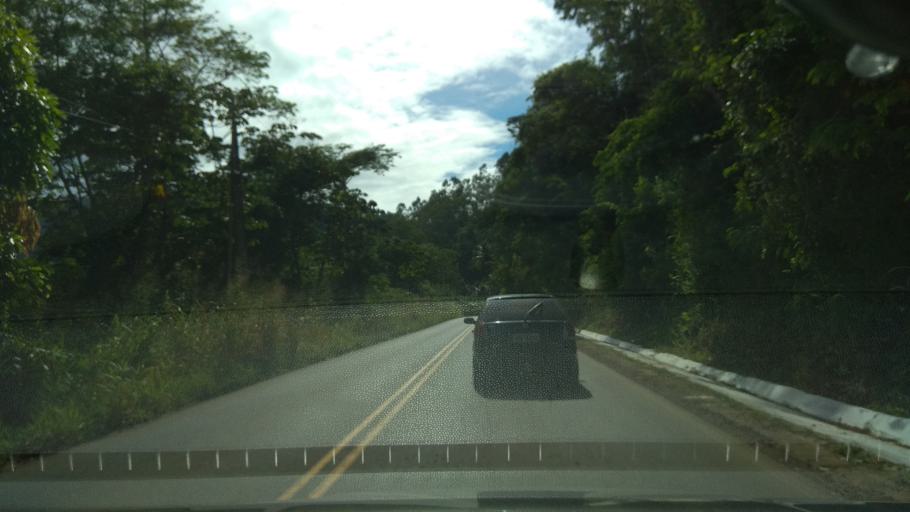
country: BR
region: Bahia
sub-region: Ubaira
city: Ubaira
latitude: -13.2638
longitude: -39.6197
